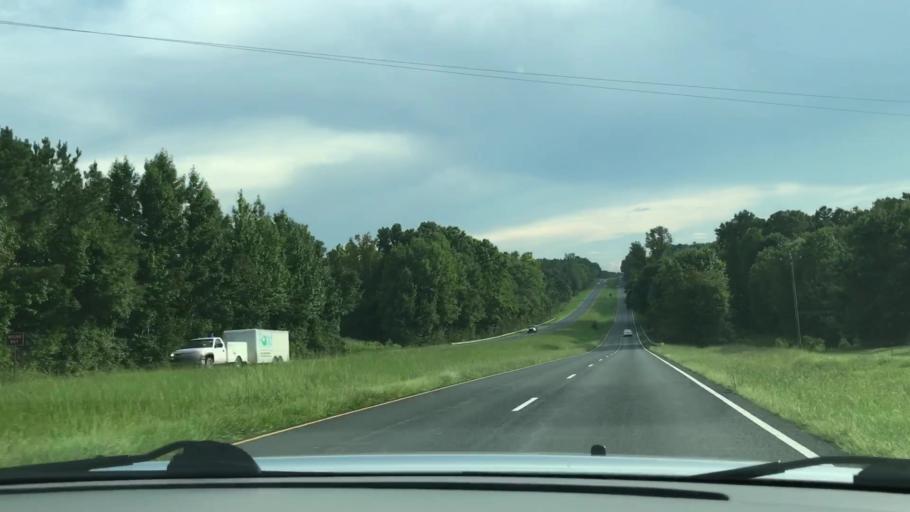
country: US
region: North Carolina
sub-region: Davidson County
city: Denton
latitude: 35.6205
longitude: -80.0102
